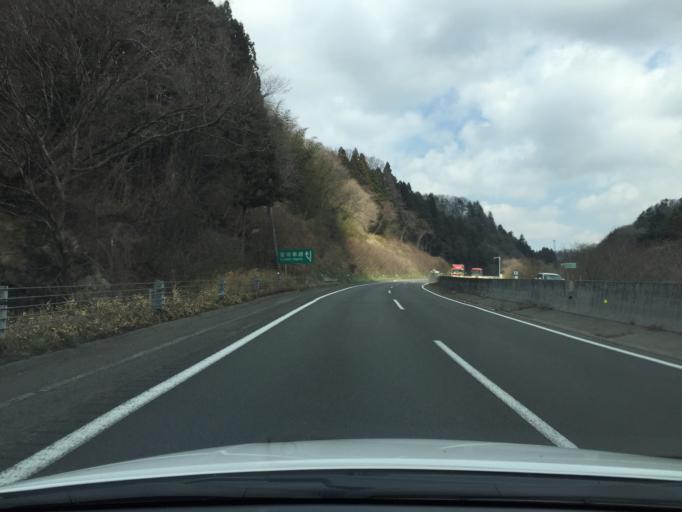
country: JP
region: Miyagi
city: Sendai
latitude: 38.2423
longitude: 140.8176
